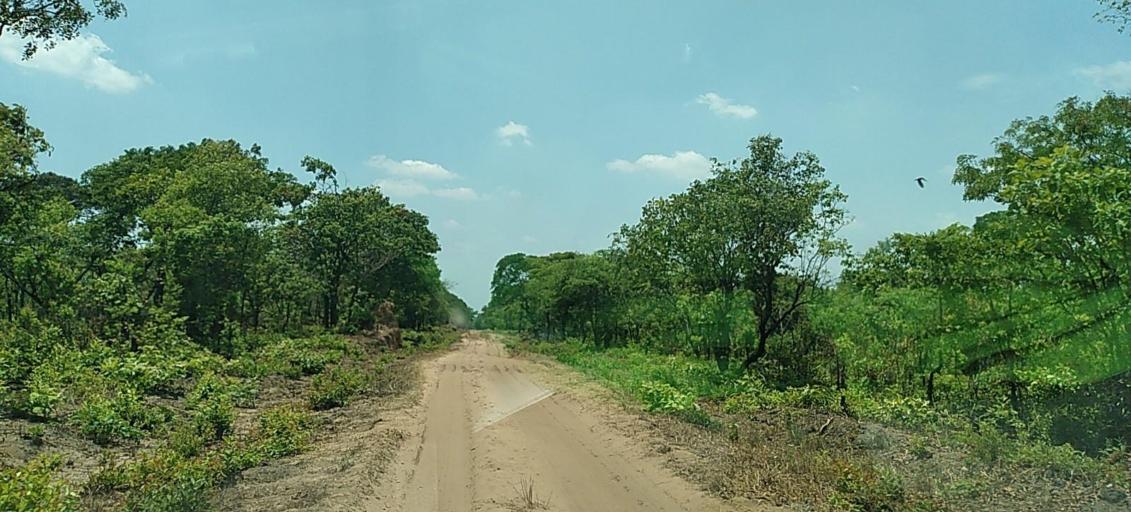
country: CD
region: Katanga
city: Kolwezi
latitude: -11.3848
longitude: 25.2196
